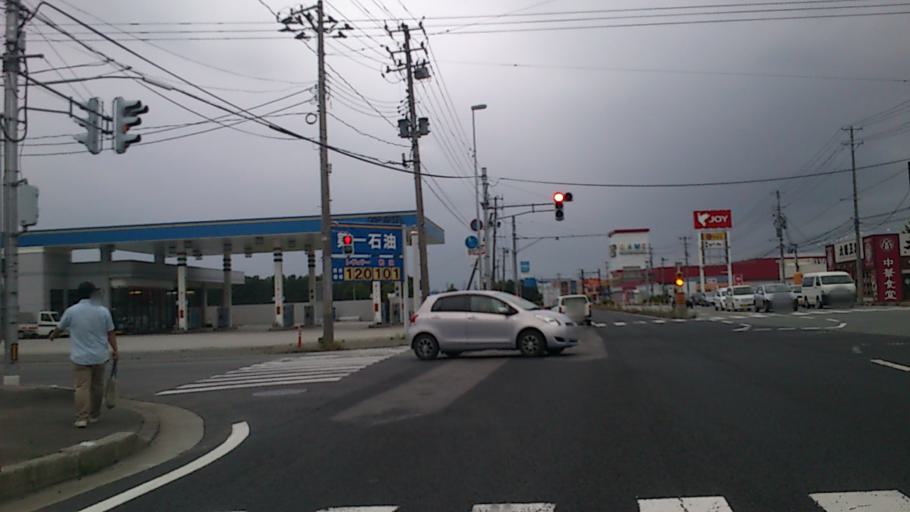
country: JP
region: Yamagata
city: Tendo
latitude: 38.3442
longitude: 140.3765
